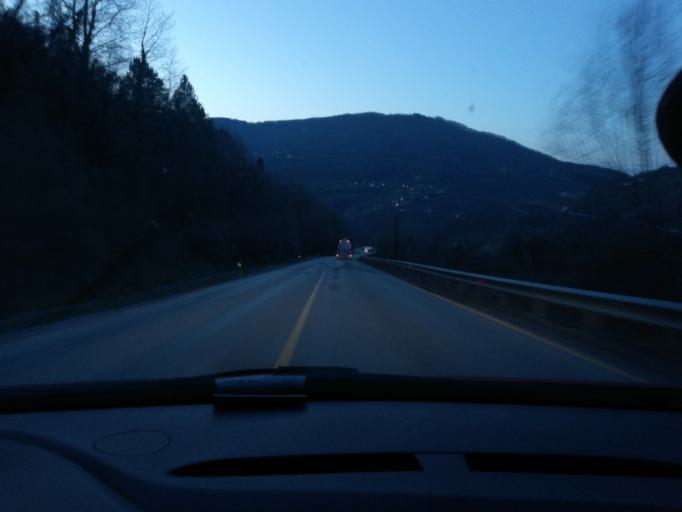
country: TR
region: Kastamonu
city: Inebolu
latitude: 41.9492
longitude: 33.7580
